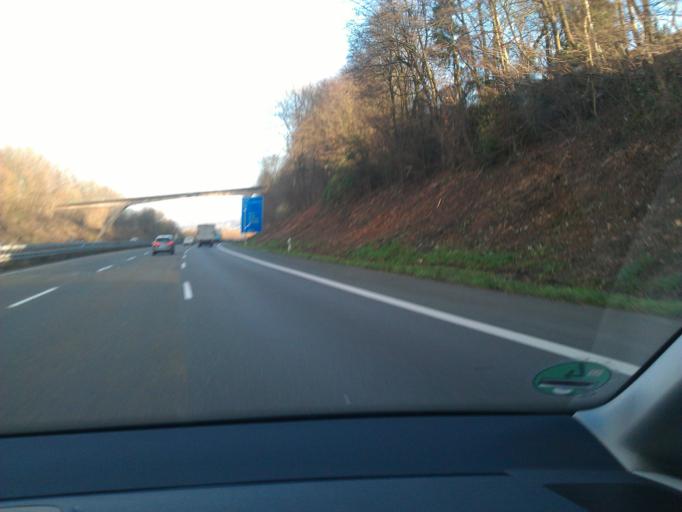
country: DE
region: North Rhine-Westphalia
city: Witten
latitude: 51.4601
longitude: 7.3721
